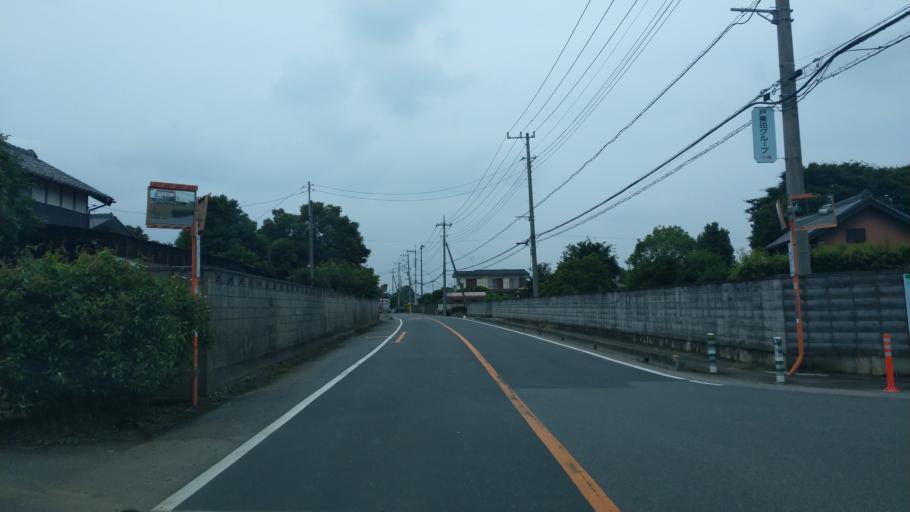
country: JP
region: Saitama
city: Iwatsuki
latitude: 35.9312
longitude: 139.6898
